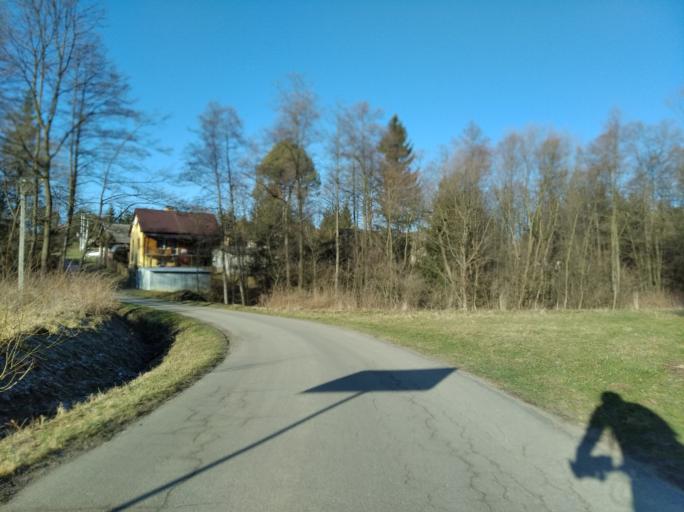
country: PL
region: Subcarpathian Voivodeship
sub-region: Powiat strzyzowski
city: Wysoka Strzyzowska
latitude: 49.8497
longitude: 21.7607
